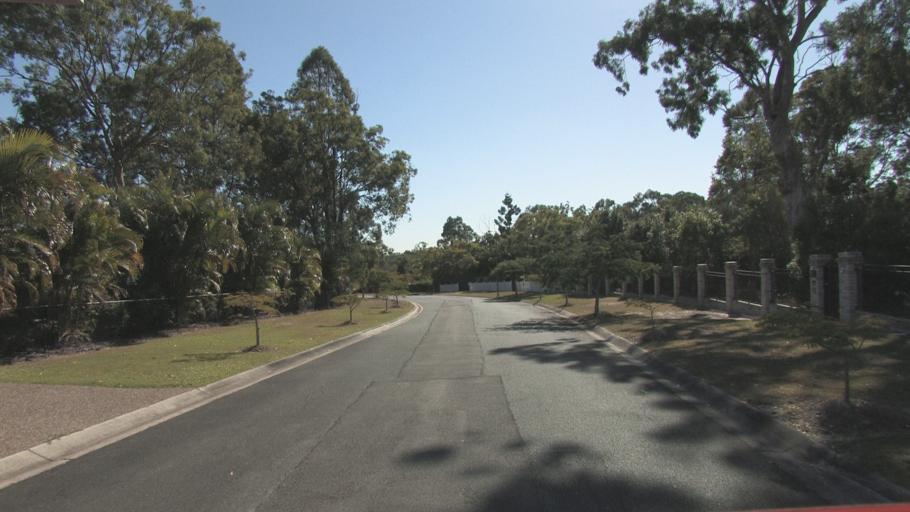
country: AU
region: Queensland
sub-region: Logan
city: Park Ridge South
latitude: -27.6663
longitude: 153.0179
